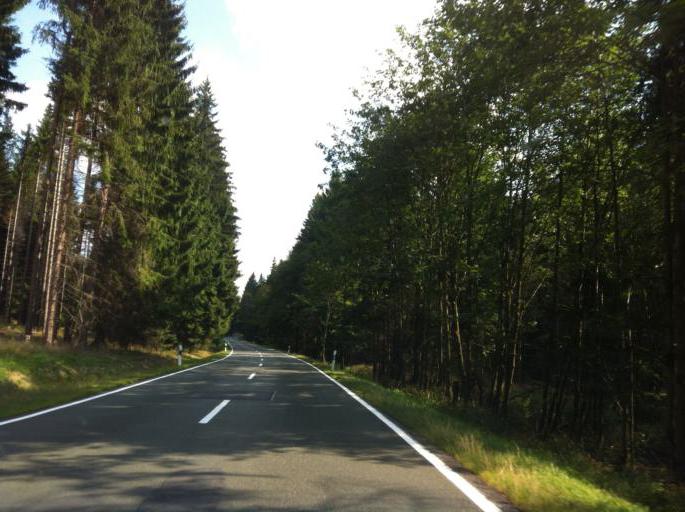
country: DE
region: Thuringia
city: Neuhaus am Rennweg
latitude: 50.5267
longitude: 11.1269
